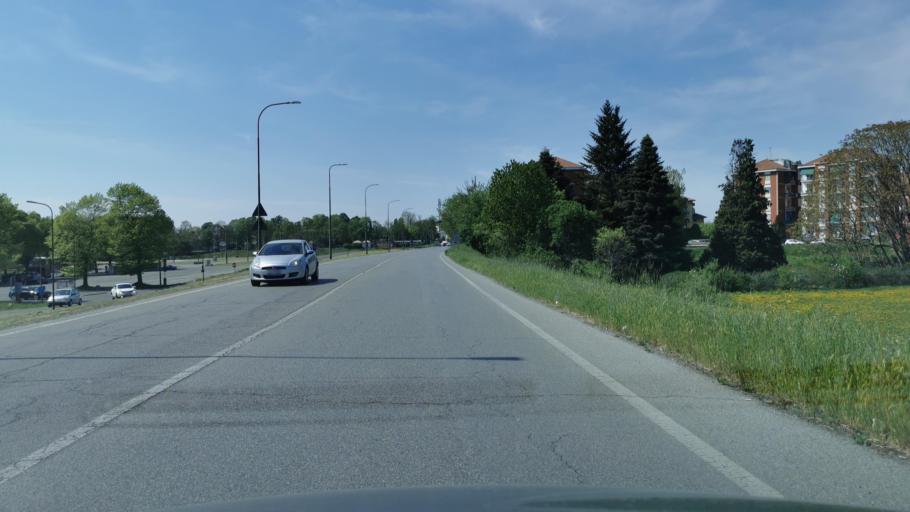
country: IT
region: Lombardy
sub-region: Provincia di Cremona
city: Cremona
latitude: 45.1286
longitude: 10.0055
